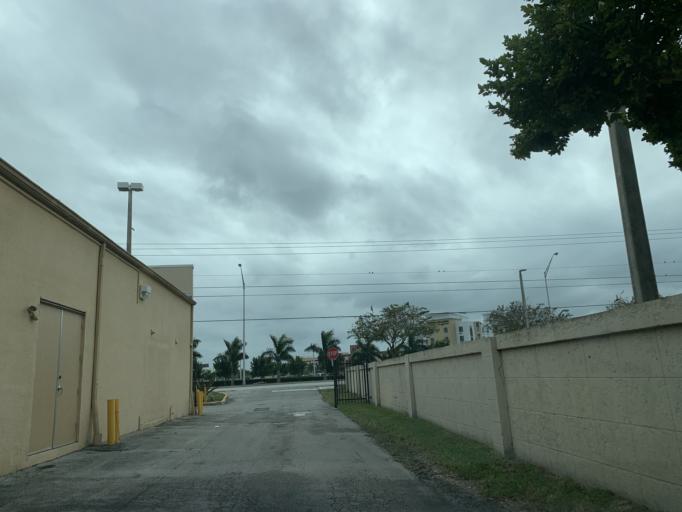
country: US
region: Florida
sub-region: Miami-Dade County
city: The Hammocks
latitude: 25.6846
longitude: -80.4560
